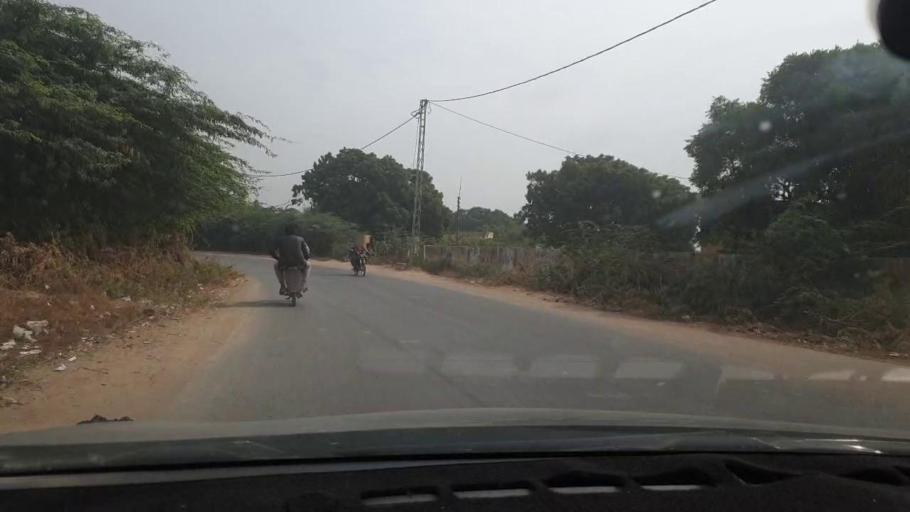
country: PK
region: Sindh
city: Malir Cantonment
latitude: 24.9139
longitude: 67.2619
